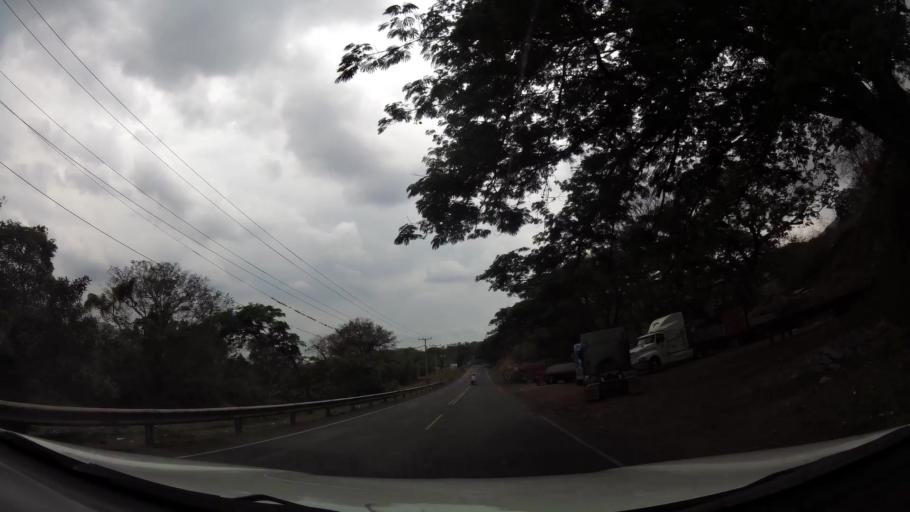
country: NI
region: Matagalpa
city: Matagalpa
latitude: 12.9150
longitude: -85.9411
